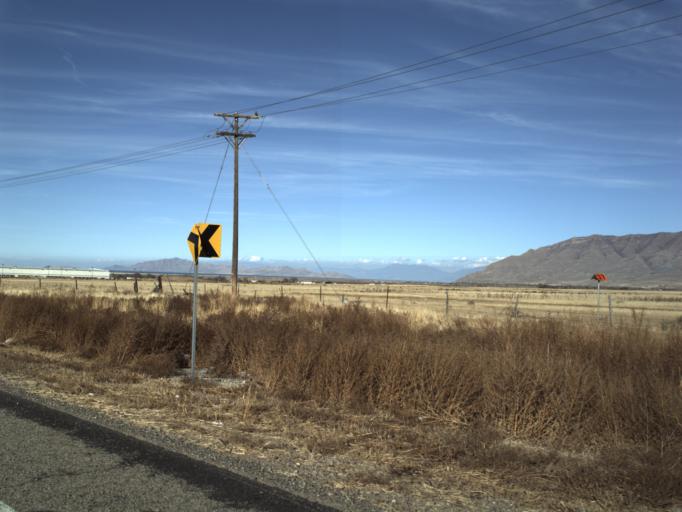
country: US
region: Utah
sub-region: Tooele County
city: Erda
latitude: 40.5777
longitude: -112.3675
